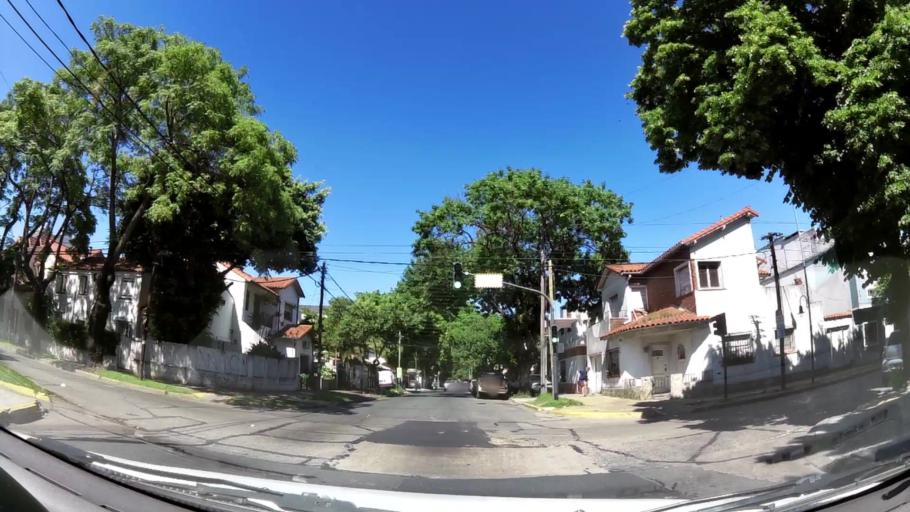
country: AR
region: Buenos Aires
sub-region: Partido de Vicente Lopez
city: Olivos
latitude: -34.5283
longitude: -58.5002
